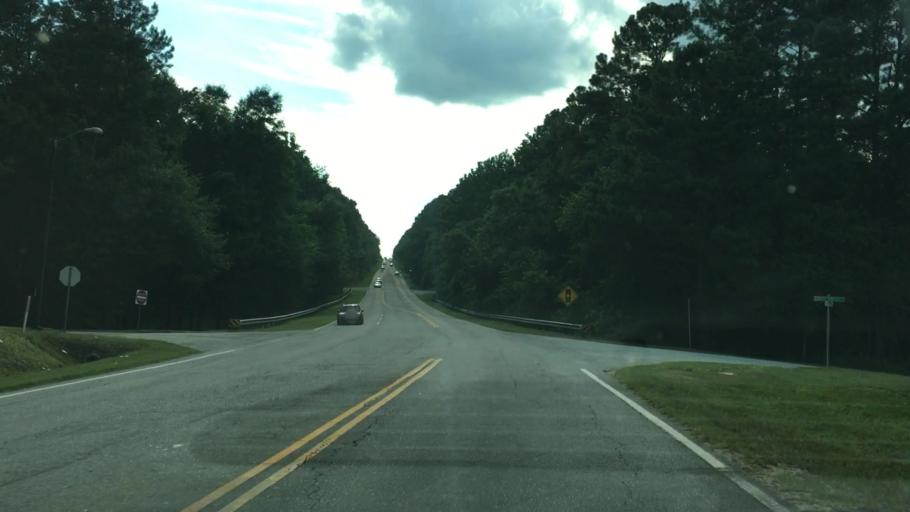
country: US
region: South Carolina
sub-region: Aiken County
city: Aiken
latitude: 33.5279
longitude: -81.7416
